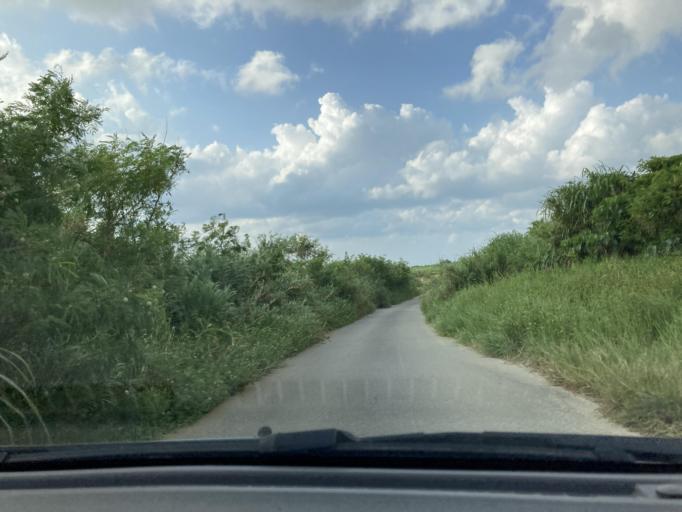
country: JP
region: Okinawa
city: Itoman
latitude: 26.0818
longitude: 127.6638
